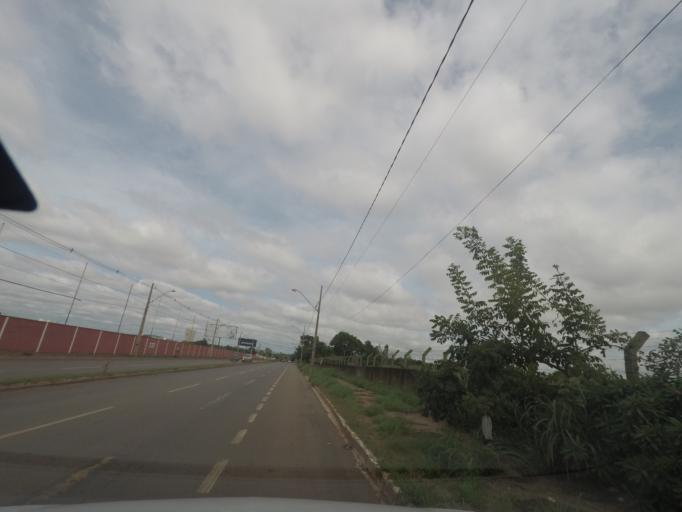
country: BR
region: Goias
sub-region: Goiania
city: Goiania
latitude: -16.6438
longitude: -49.2135
